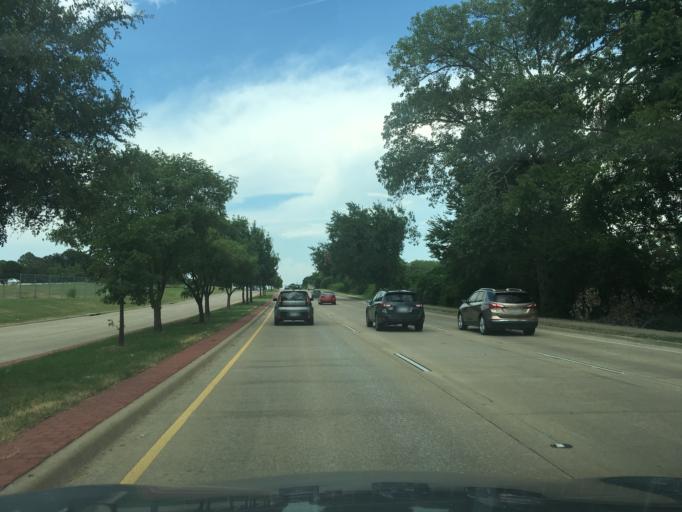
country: US
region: Texas
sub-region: Denton County
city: Denton
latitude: 33.2312
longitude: -97.1231
